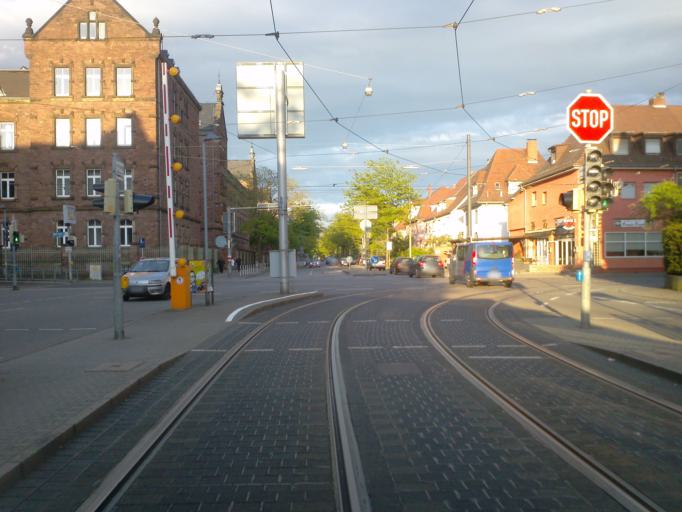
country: DE
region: Baden-Wuerttemberg
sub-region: Karlsruhe Region
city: Karlsruhe
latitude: 49.0151
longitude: 8.3747
